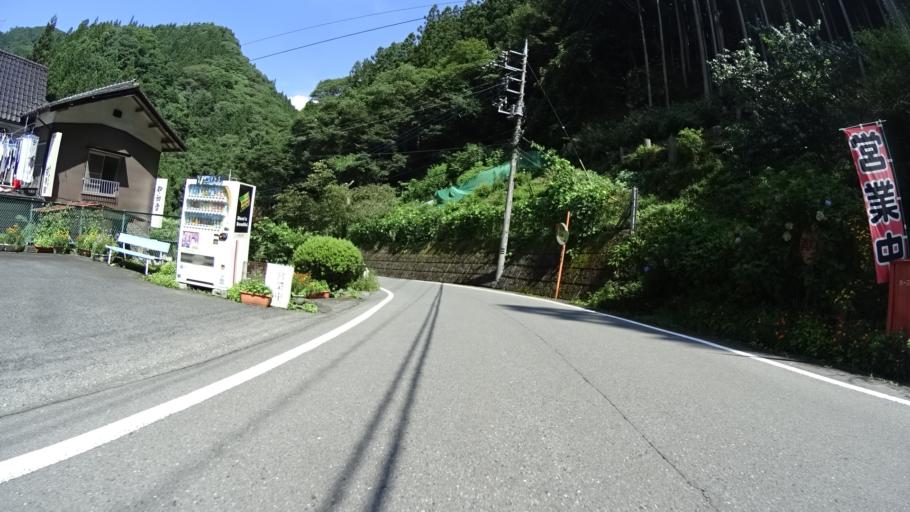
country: JP
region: Gunma
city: Tomioka
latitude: 36.0665
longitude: 138.8317
